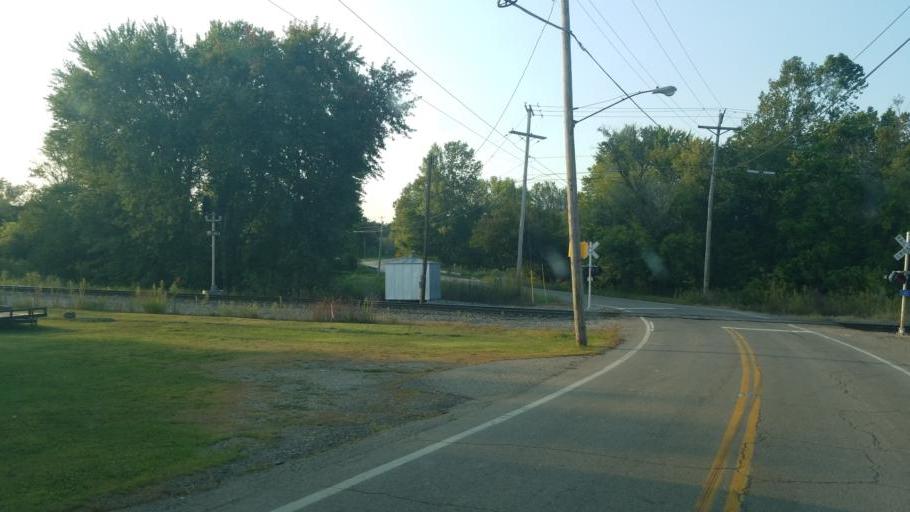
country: US
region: Ohio
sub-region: Wayne County
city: Shreve
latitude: 40.6678
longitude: -82.0954
